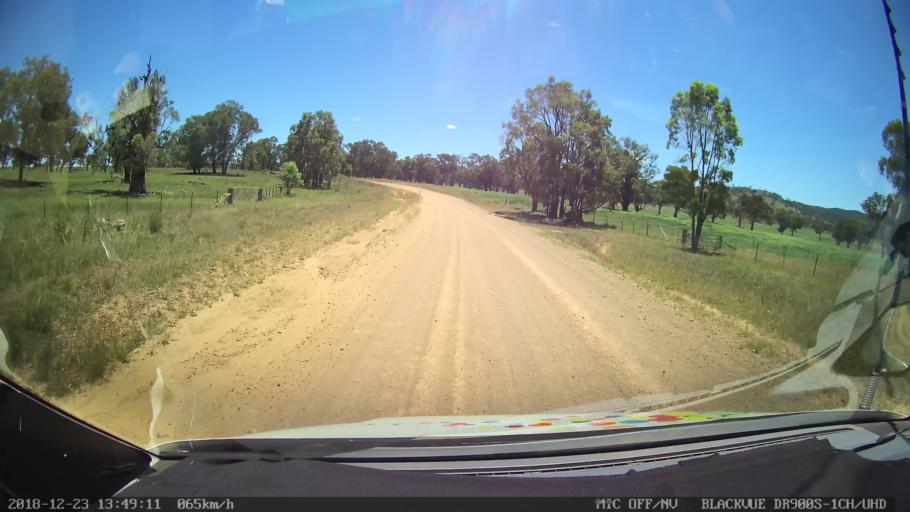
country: AU
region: New South Wales
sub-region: Tamworth Municipality
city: Manilla
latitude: -30.5204
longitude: 151.1102
